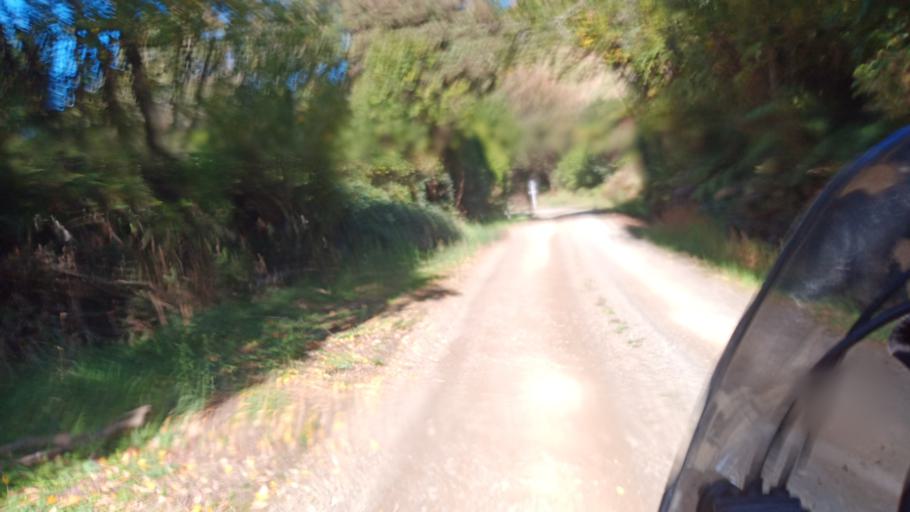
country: NZ
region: Bay of Plenty
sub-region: Opotiki District
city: Opotiki
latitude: -38.2485
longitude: 177.5944
